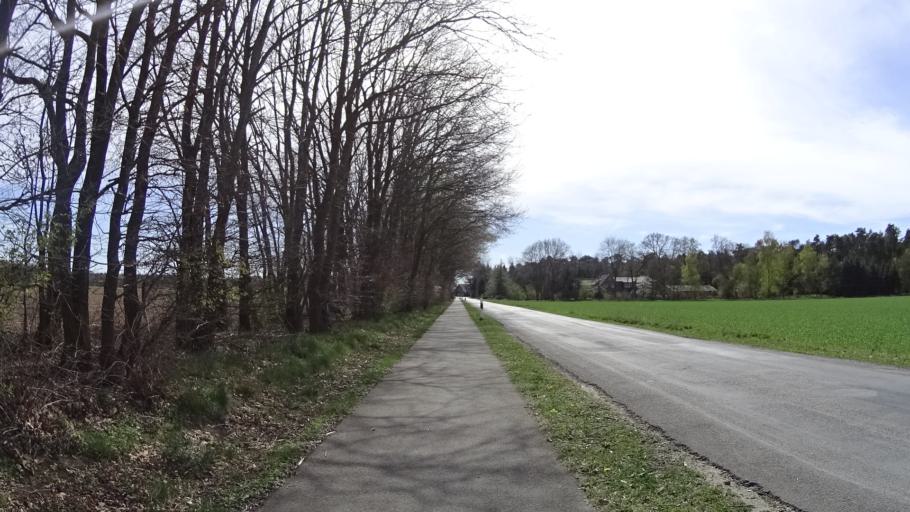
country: DE
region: Lower Saxony
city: Spelle
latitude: 52.3525
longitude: 7.4443
